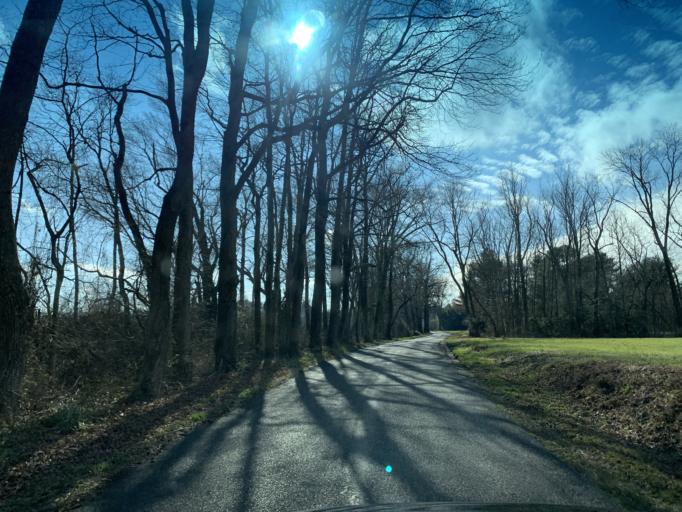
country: US
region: Delaware
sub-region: Sussex County
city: Selbyville
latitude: 38.4441
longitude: -75.1893
